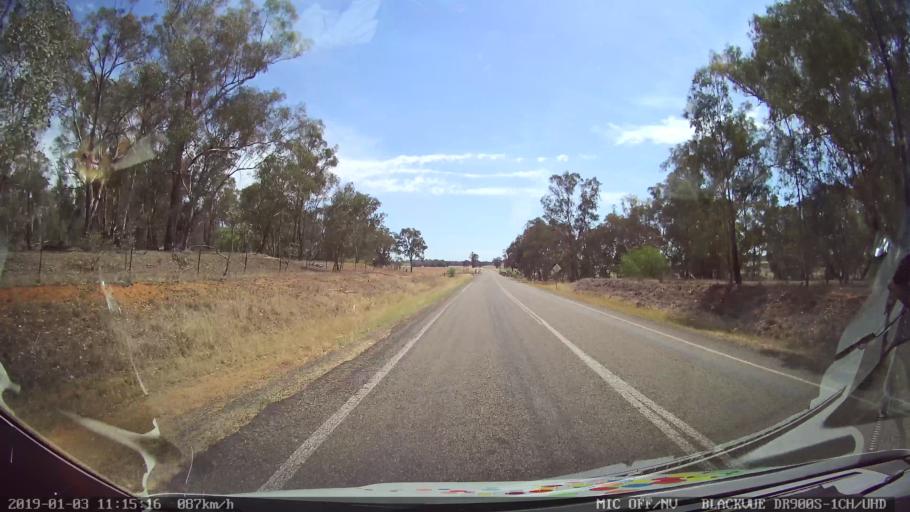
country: AU
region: New South Wales
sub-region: Young
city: Young
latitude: -34.1658
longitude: 148.2632
